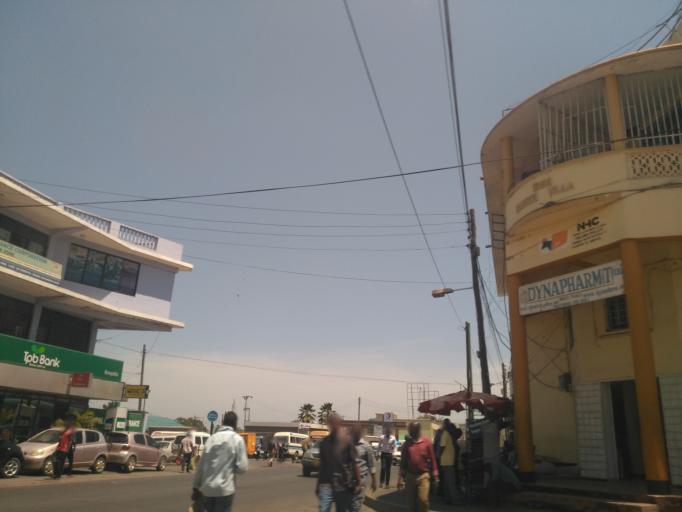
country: TZ
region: Mwanza
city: Mwanza
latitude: -2.5244
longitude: 32.9005
